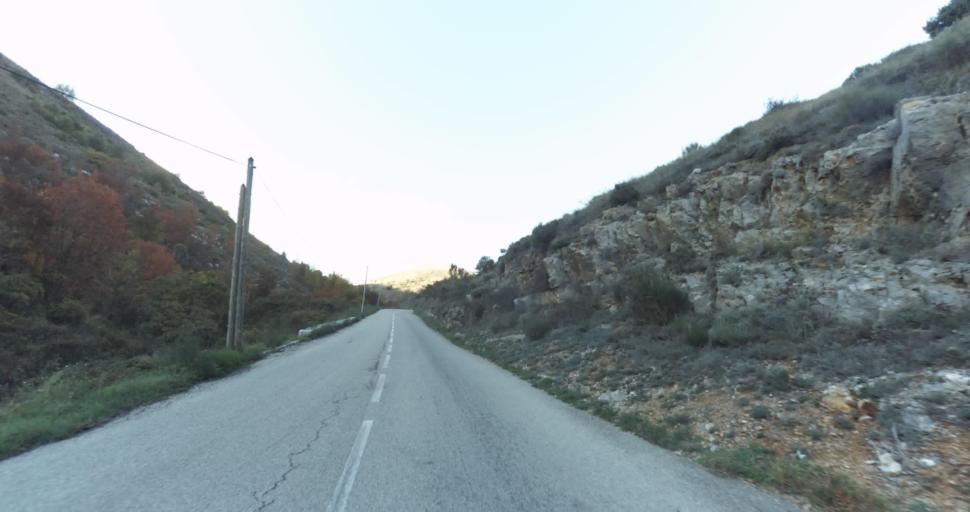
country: FR
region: Provence-Alpes-Cote d'Azur
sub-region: Departement des Alpes-Maritimes
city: Vence
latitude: 43.7425
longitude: 7.1046
